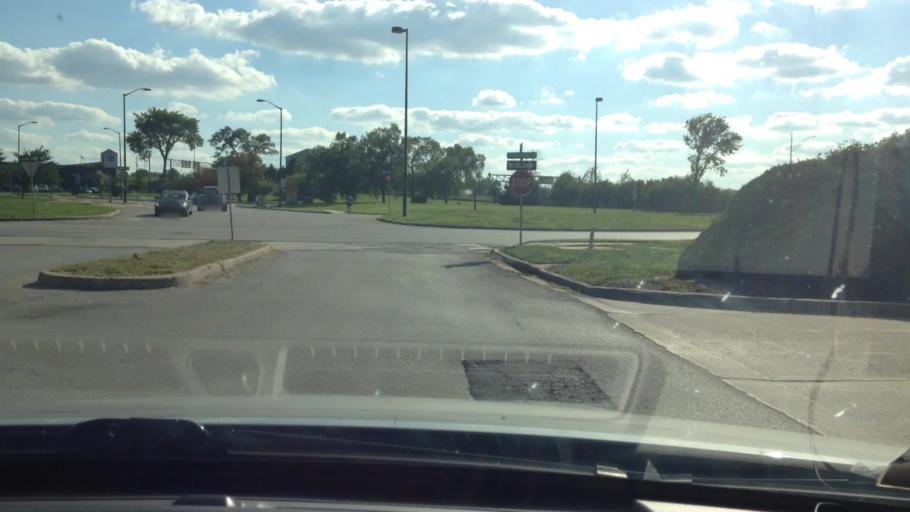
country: US
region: Missouri
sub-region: Platte County
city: Weatherby Lake
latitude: 39.2743
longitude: -94.6657
